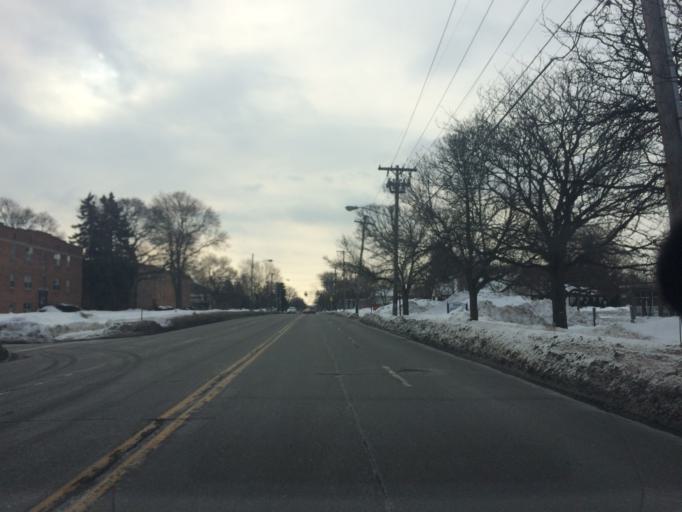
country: US
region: New York
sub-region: Monroe County
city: Brighton
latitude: 43.1251
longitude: -77.5631
